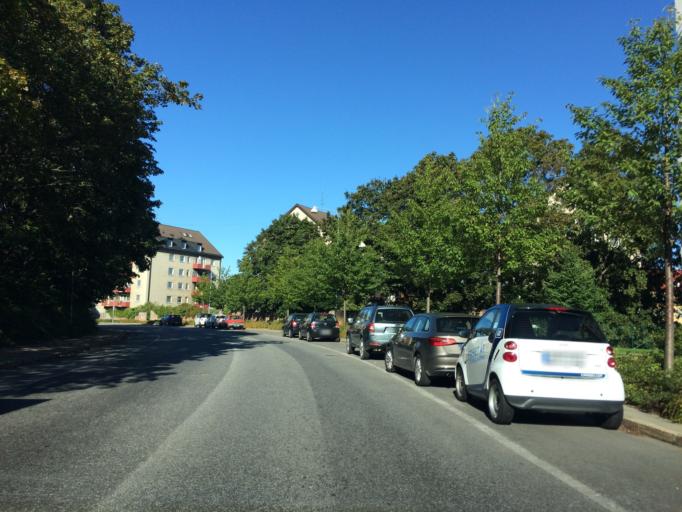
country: SE
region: Stockholm
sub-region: Solna Kommun
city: Solna
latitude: 59.3531
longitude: 18.0033
